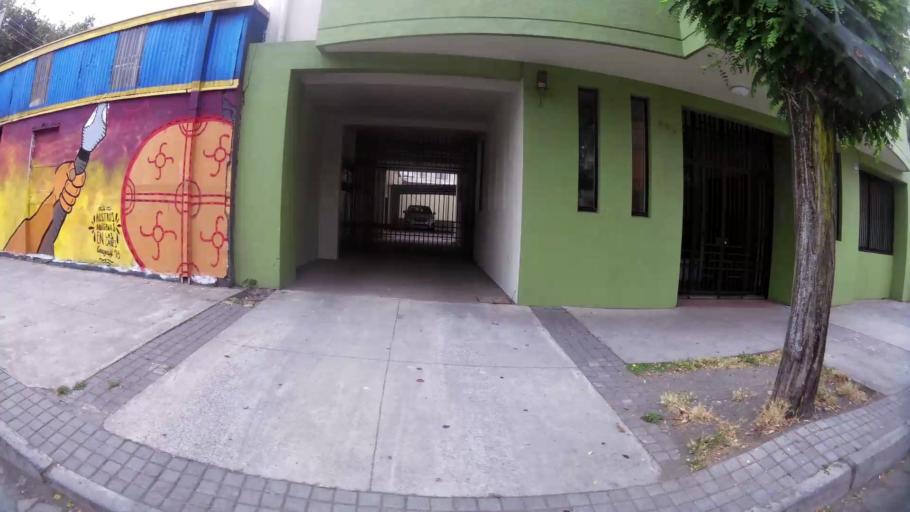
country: CL
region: Biobio
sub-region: Provincia de Concepcion
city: Concepcion
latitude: -36.8187
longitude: -73.0435
